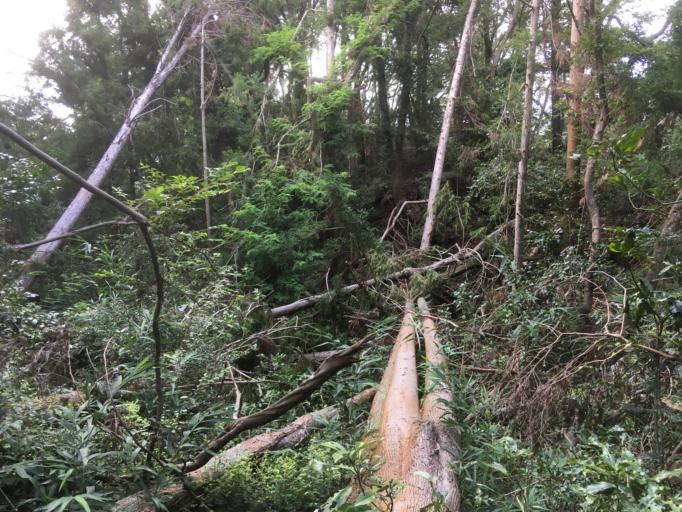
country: JP
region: Nara
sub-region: Ikoma-shi
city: Ikoma
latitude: 34.6979
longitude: 135.6640
